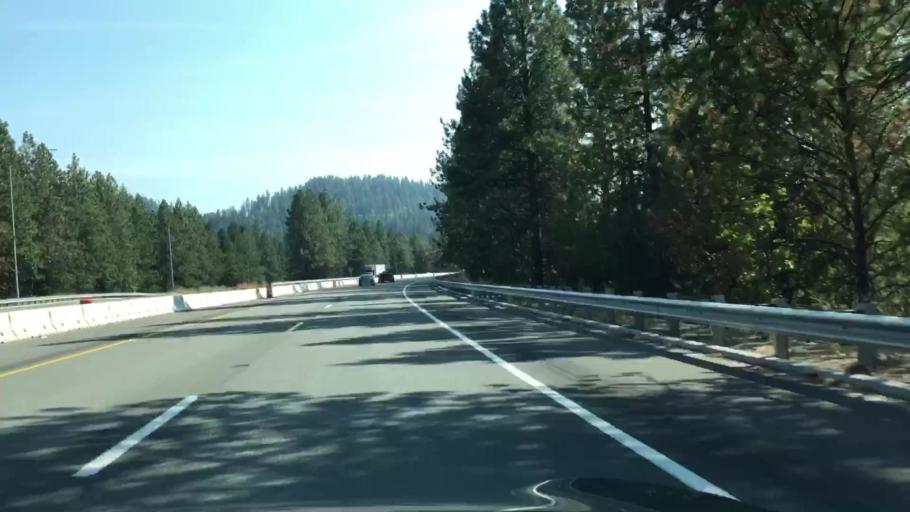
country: US
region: Idaho
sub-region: Kootenai County
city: Coeur d'Alene
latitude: 47.6764
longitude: -116.7529
